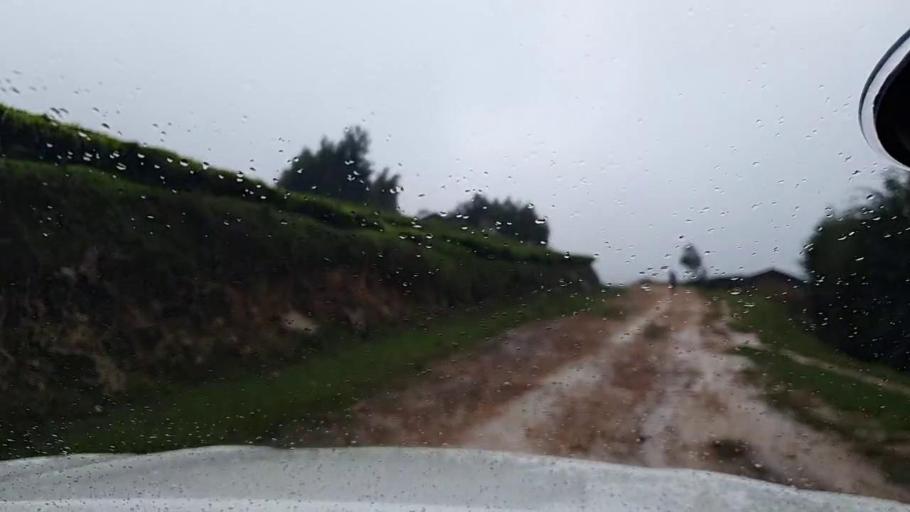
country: RW
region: Western Province
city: Kibuye
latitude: -2.1352
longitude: 29.4683
